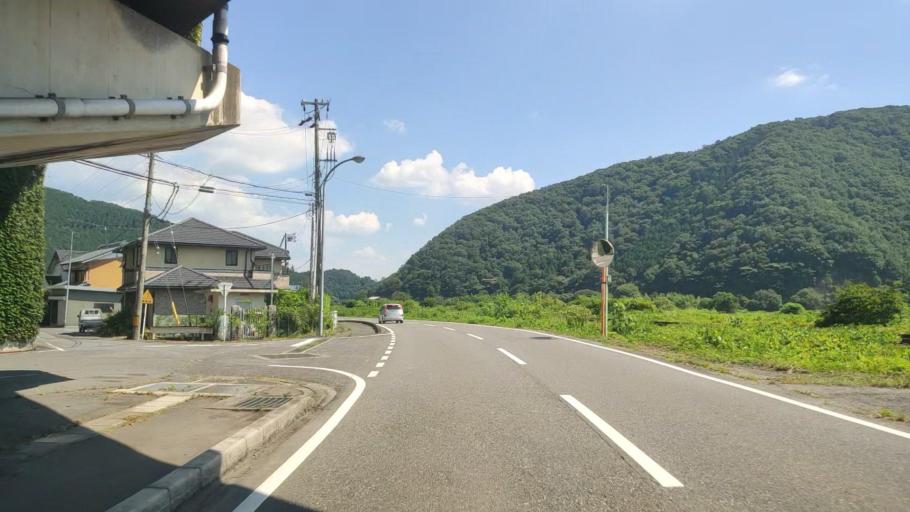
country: JP
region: Gifu
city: Godo
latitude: 35.5211
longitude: 136.6447
